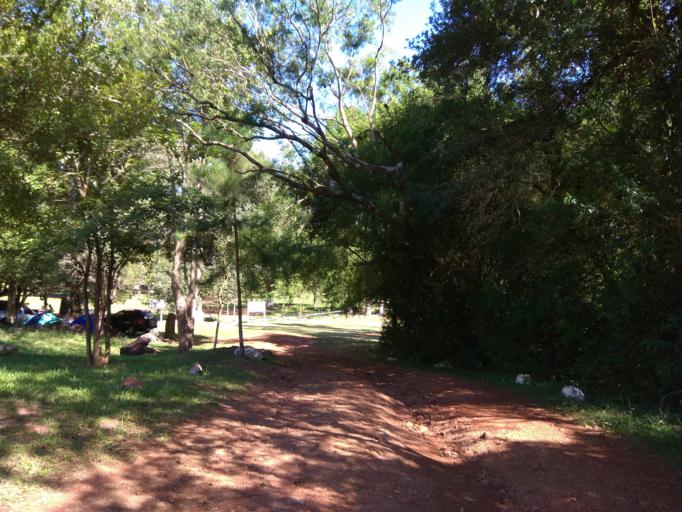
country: AR
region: Misiones
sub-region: Departamento de Apostoles
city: Apostoles
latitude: -27.9847
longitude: -55.7846
